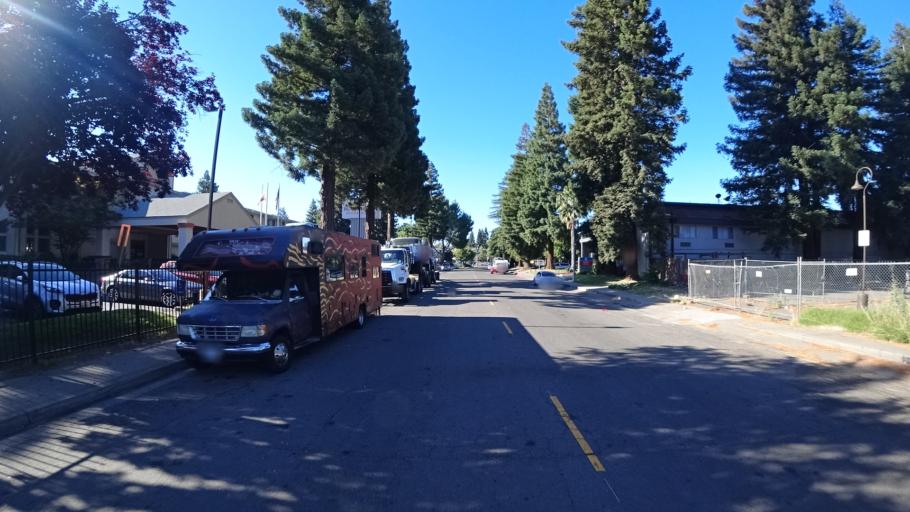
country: US
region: California
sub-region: Sacramento County
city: Sacramento
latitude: 38.5987
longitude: -121.5025
